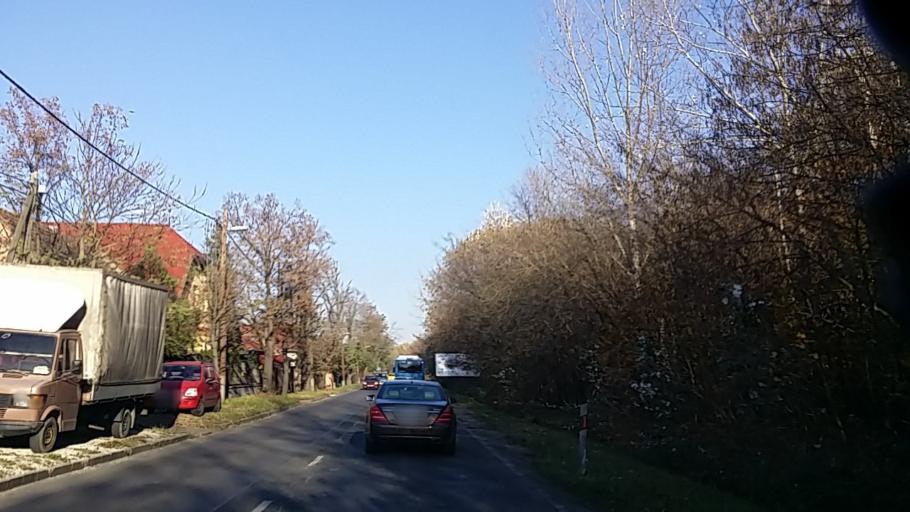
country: HU
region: Budapest
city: Budapest XVIII. keruelet
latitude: 47.4551
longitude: 19.1994
